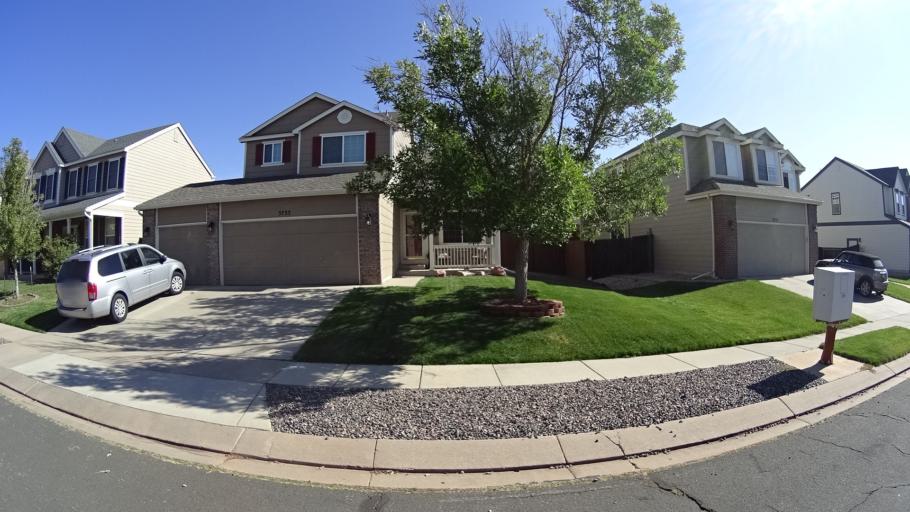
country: US
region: Colorado
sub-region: El Paso County
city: Cimarron Hills
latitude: 38.8854
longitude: -104.7093
